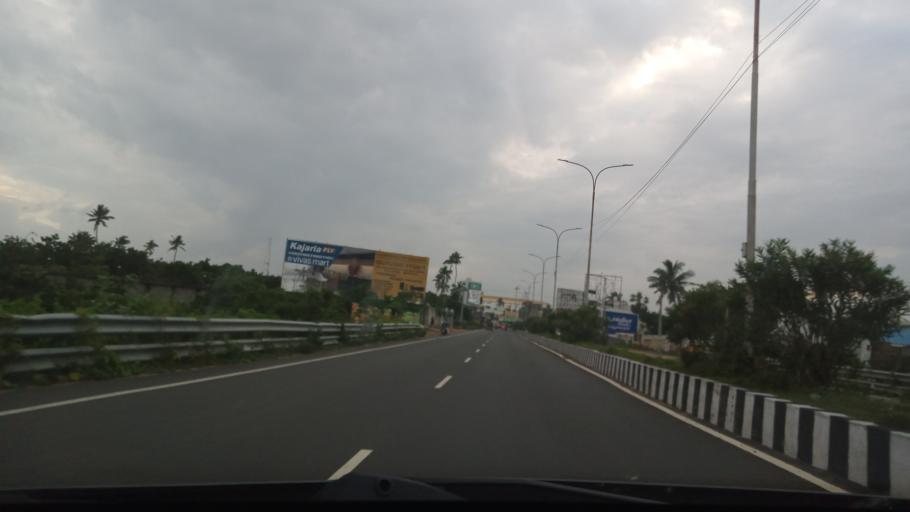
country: IN
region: Pondicherry
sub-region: Puducherry
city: Puducherry
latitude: 11.9607
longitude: 79.8306
